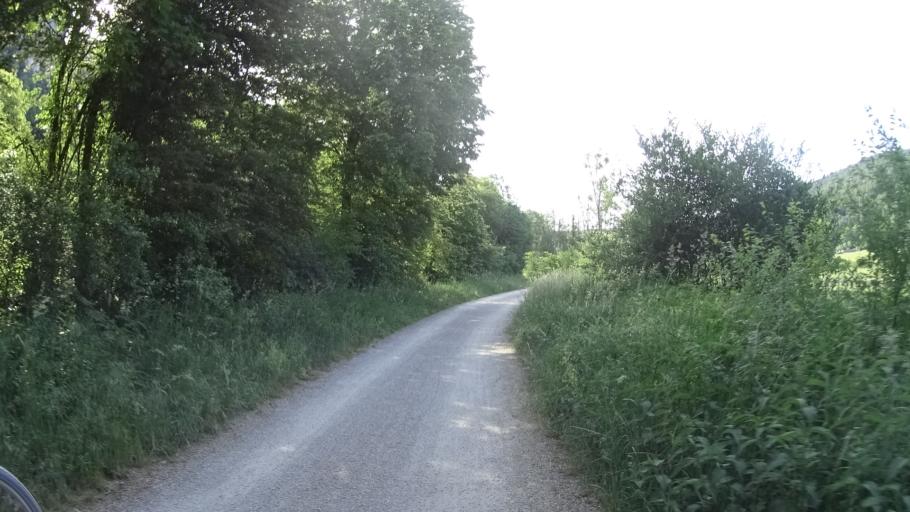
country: DE
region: Bavaria
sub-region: Lower Bavaria
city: Riedenburg
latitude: 48.9501
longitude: 11.7372
